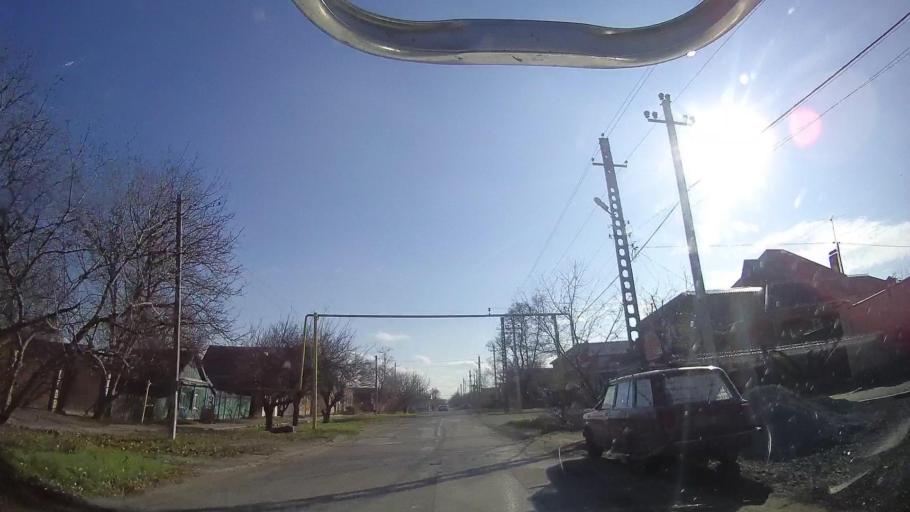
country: RU
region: Rostov
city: Bataysk
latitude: 47.1173
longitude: 39.6831
